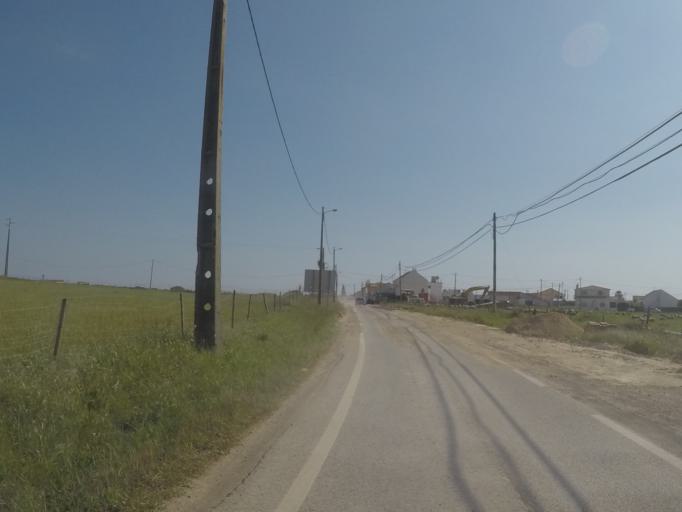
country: PT
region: Setubal
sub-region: Sesimbra
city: Sesimbra
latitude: 38.4335
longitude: -9.1833
